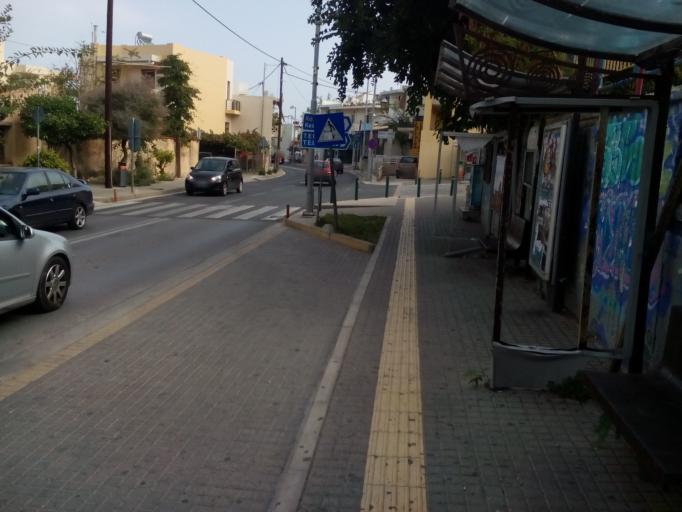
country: GR
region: Crete
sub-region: Nomos Rethymnis
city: Rethymno
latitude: 35.3664
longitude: 24.5019
